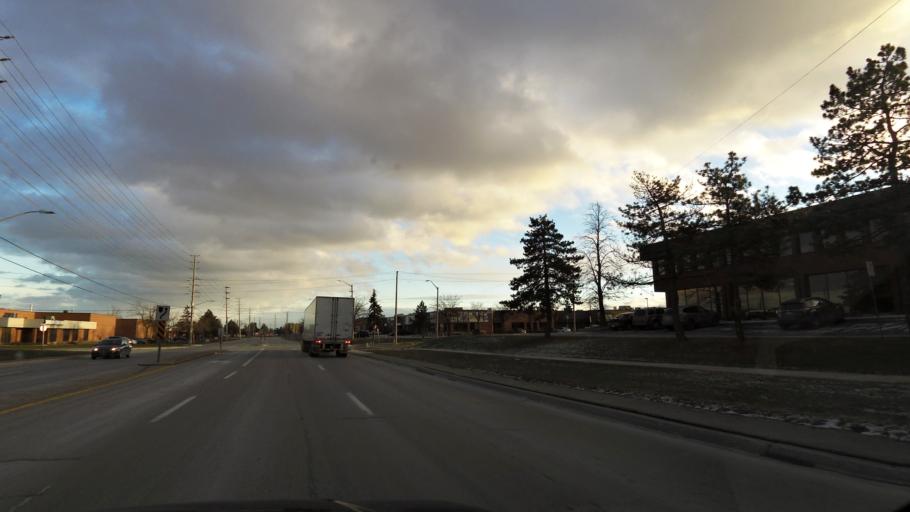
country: CA
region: Ontario
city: Mississauga
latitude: 43.6312
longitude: -79.6385
